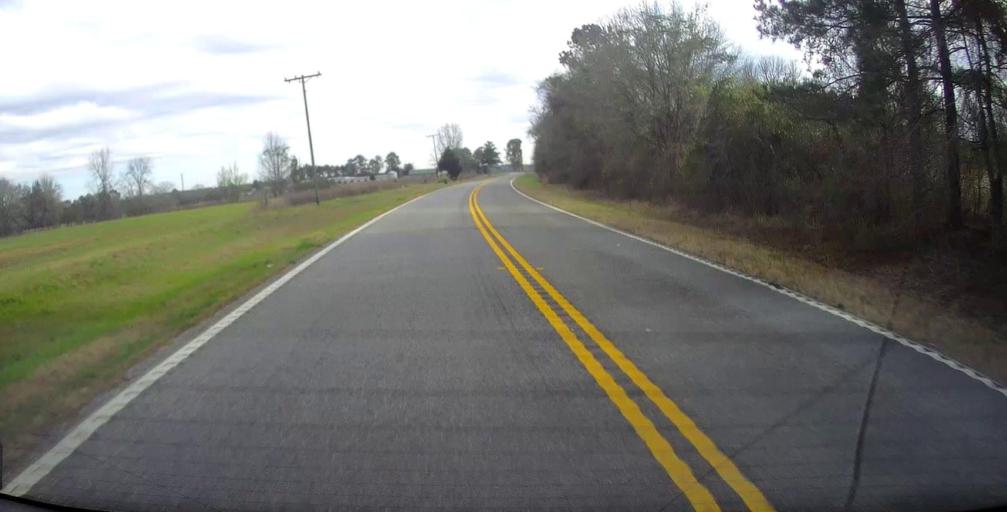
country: US
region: Georgia
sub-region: Marion County
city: Buena Vista
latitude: 32.4478
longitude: -84.4409
